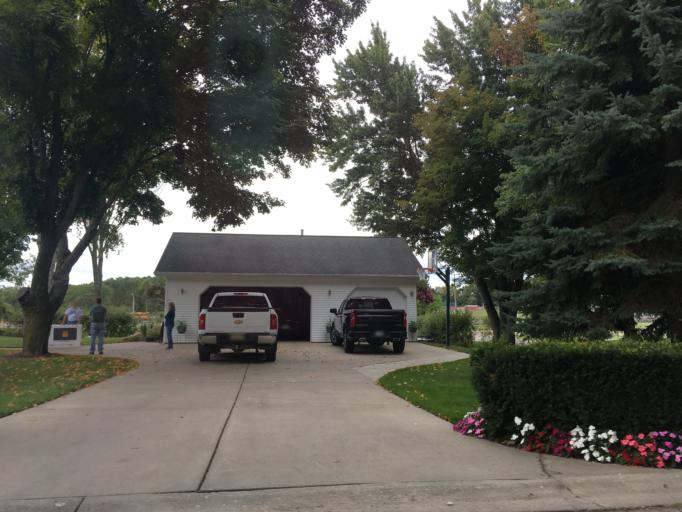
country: US
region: Michigan
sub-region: Lapeer County
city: Barnes Lake-Millers Lake
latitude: 43.3335
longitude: -83.3548
